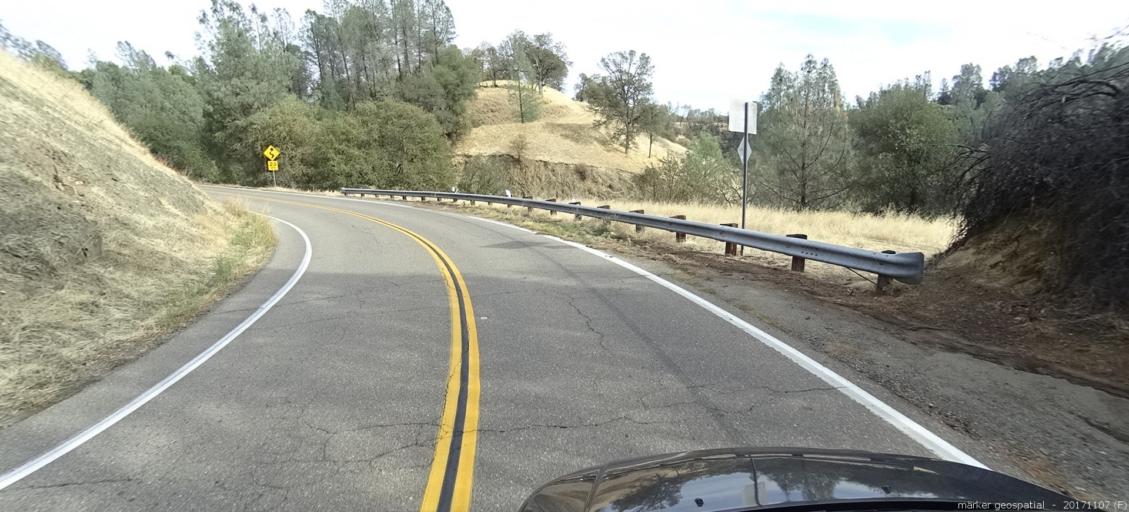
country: US
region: California
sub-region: Shasta County
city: Shasta
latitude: 40.5117
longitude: -122.5208
